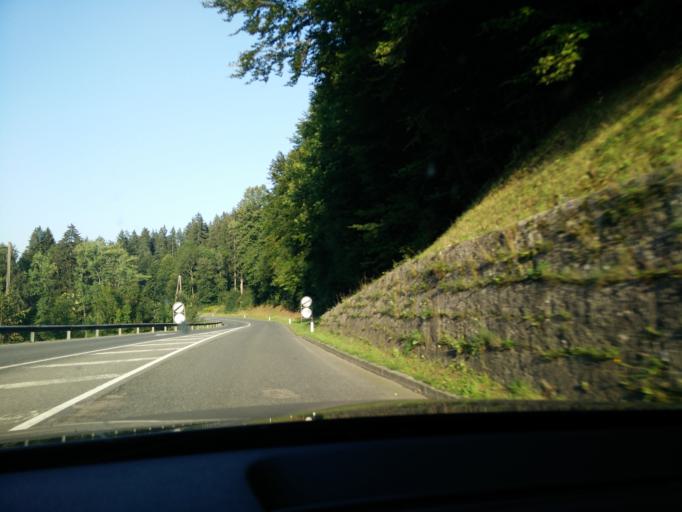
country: AT
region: Carinthia
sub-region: Politischer Bezirk Klagenfurt Land
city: Kottmannsdorf
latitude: 46.5499
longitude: 14.2622
